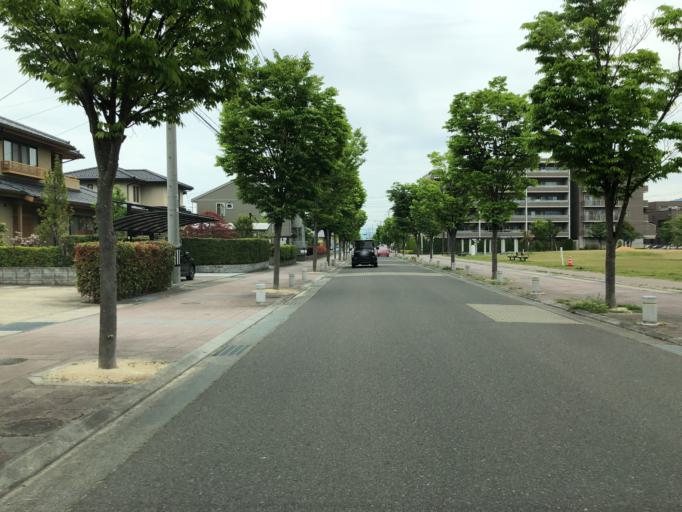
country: JP
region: Fukushima
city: Fukushima-shi
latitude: 37.7914
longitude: 140.4486
